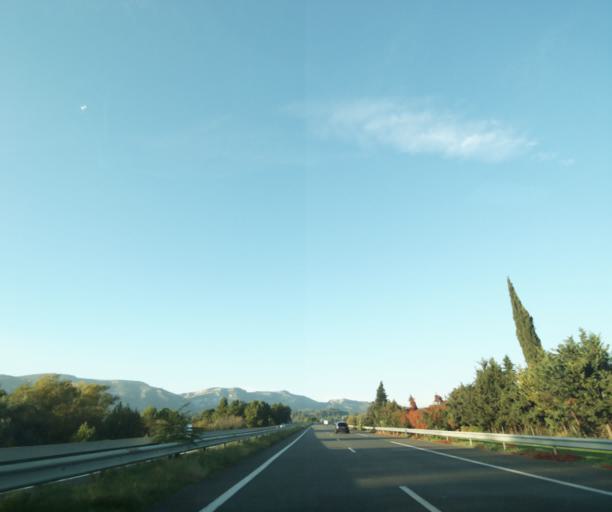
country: FR
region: Provence-Alpes-Cote d'Azur
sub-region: Departement des Bouches-du-Rhone
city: Aubagne
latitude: 43.3143
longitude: 5.5911
